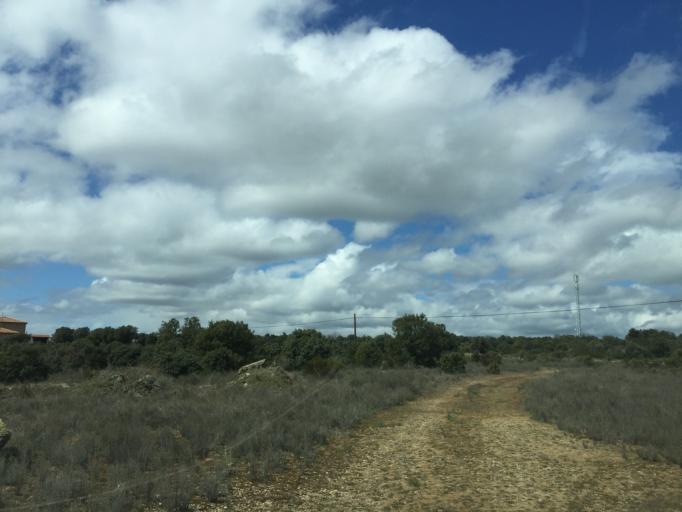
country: ES
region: Castille and Leon
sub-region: Provincia de Zamora
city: Torregamones
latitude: 41.4783
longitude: -6.1797
